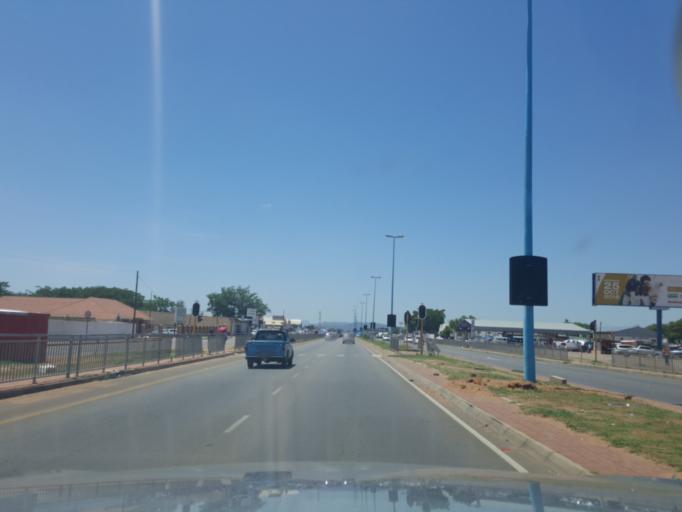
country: BW
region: Kweneng
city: Mogoditshane
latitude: -24.6146
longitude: 25.8627
